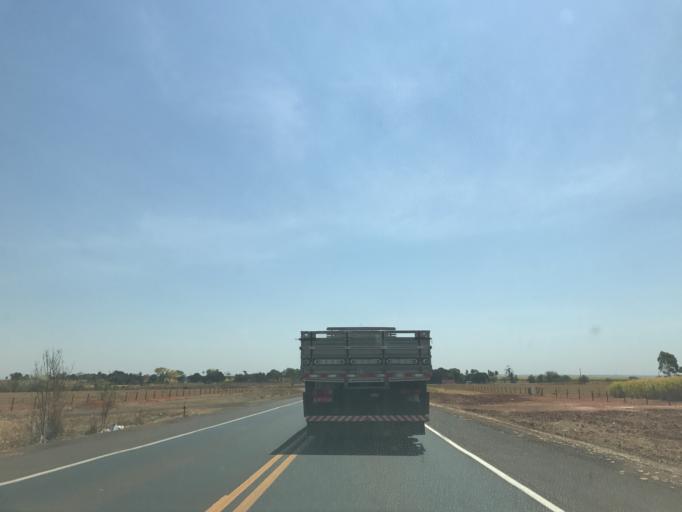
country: BR
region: Minas Gerais
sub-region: Frutal
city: Frutal
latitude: -20.0248
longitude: -49.0479
